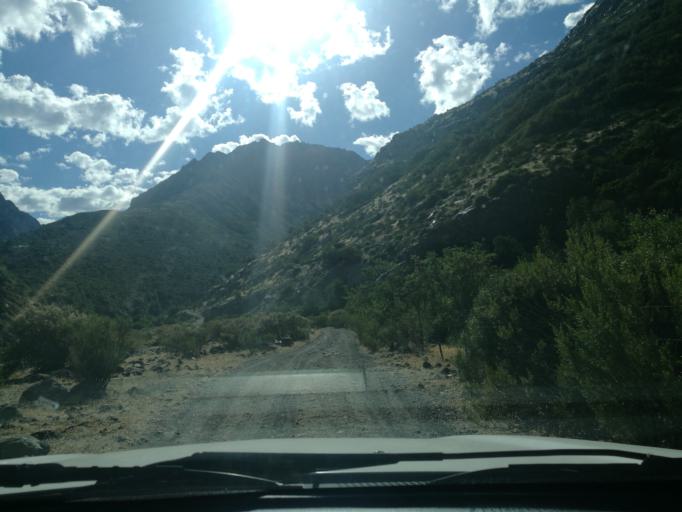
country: CL
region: O'Higgins
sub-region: Provincia de Cachapoal
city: Machali
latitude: -34.3643
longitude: -70.3126
